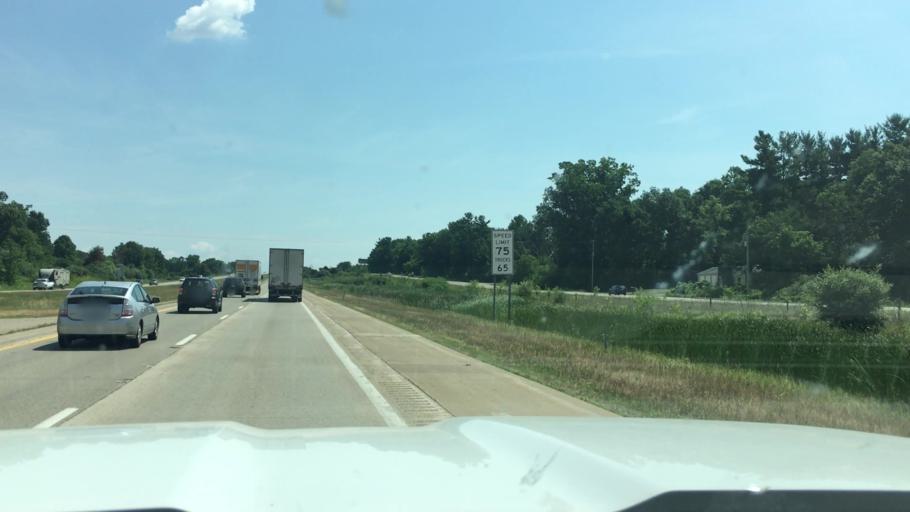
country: US
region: Michigan
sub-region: Ingham County
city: Haslett
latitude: 42.8030
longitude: -84.3354
